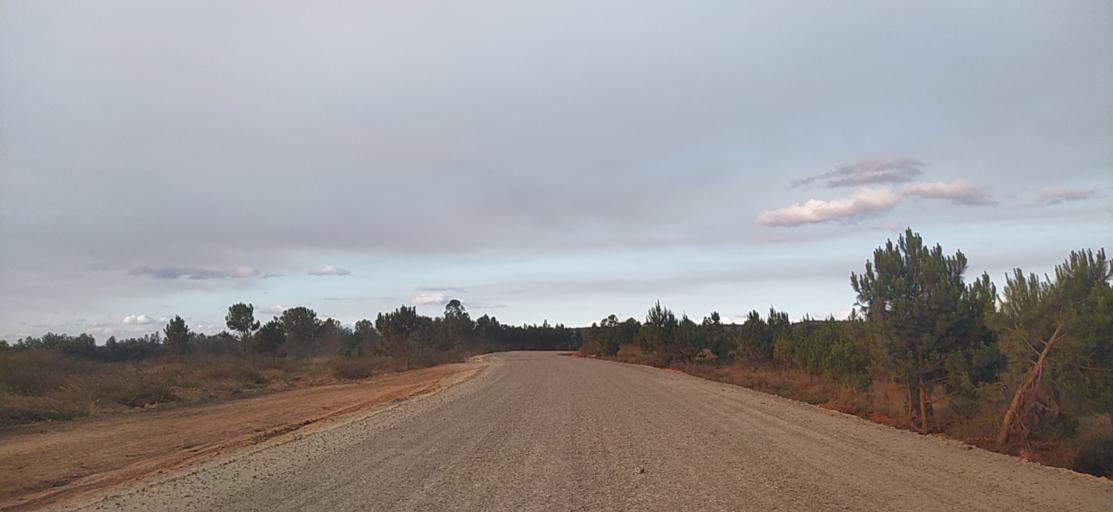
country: MG
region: Analamanga
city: Anjozorobe
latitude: -18.5067
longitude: 48.2634
